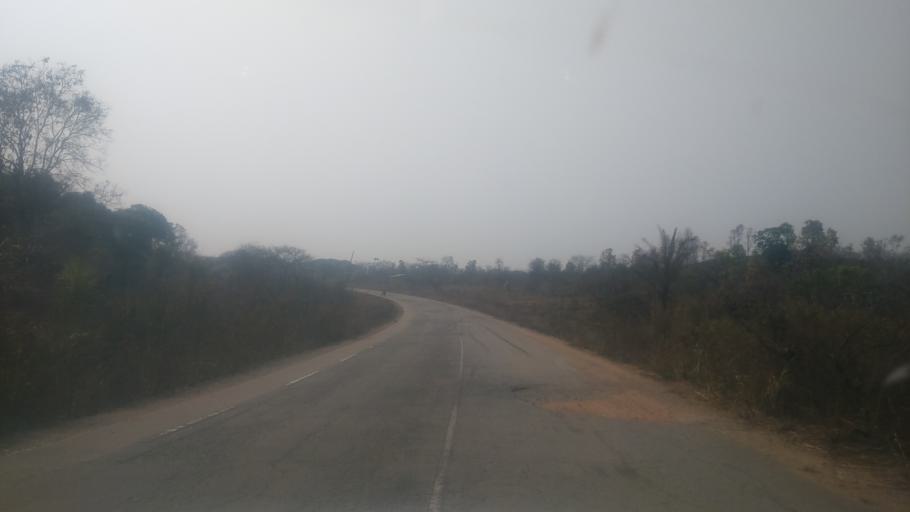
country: CM
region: Centre
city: Ndikinimeki
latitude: 4.8053
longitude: 10.9883
